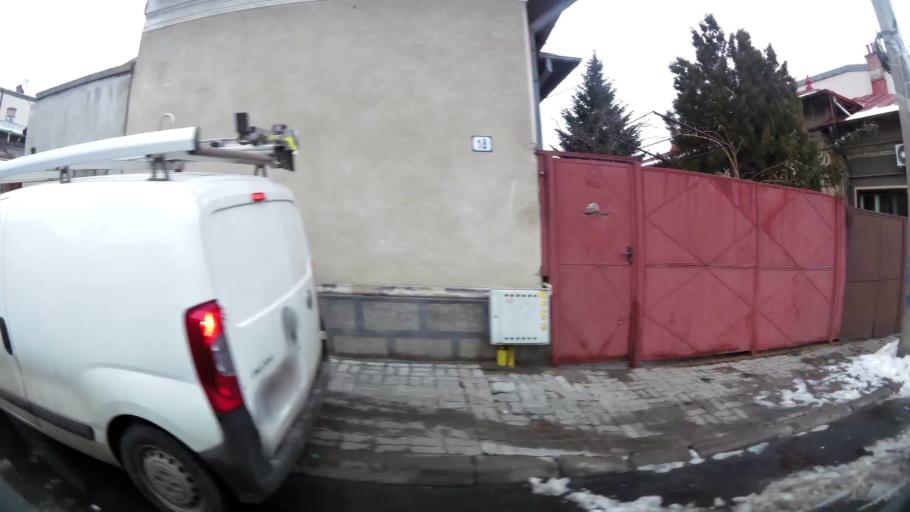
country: RO
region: Bucuresti
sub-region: Municipiul Bucuresti
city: Bucuresti
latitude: 44.4559
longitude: 26.0686
